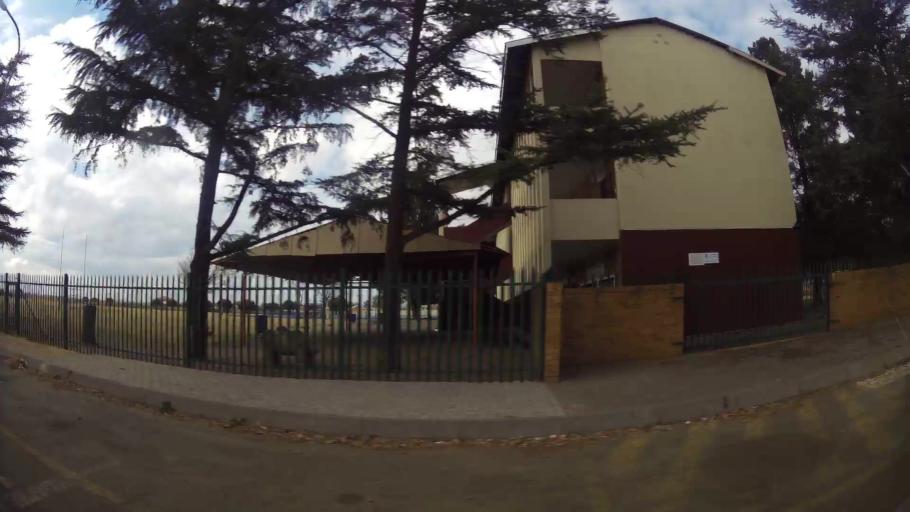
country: ZA
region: Gauteng
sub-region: Sedibeng District Municipality
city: Meyerton
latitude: -26.6011
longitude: 28.0465
